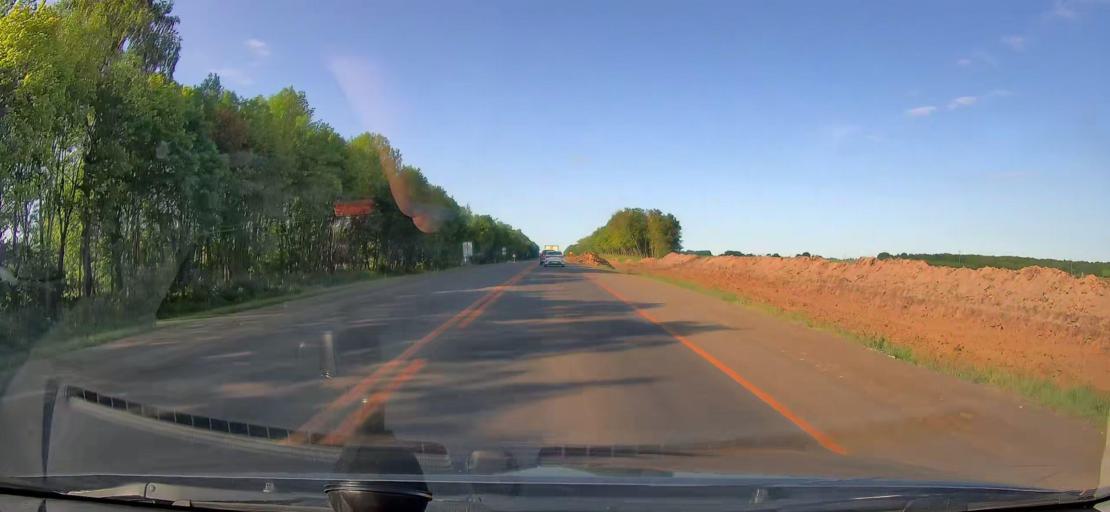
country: RU
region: Tula
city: Bol'shoye Skuratovo
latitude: 53.4109
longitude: 36.7756
